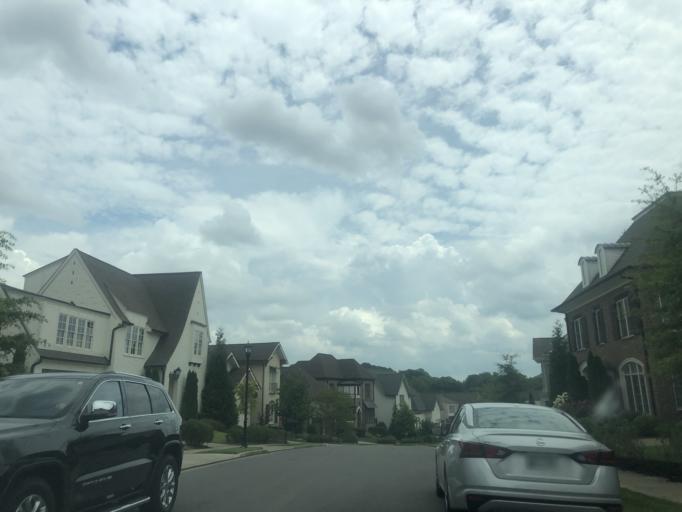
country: US
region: Tennessee
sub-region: Davidson County
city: Oak Hill
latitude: 36.0976
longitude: -86.7956
